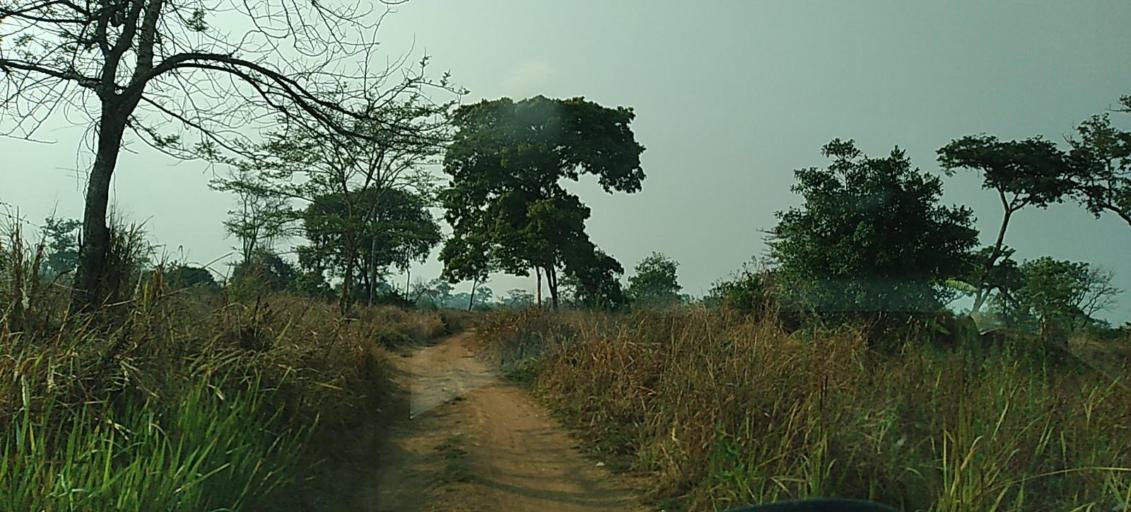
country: ZM
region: North-Western
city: Solwezi
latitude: -12.3596
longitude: 26.5525
